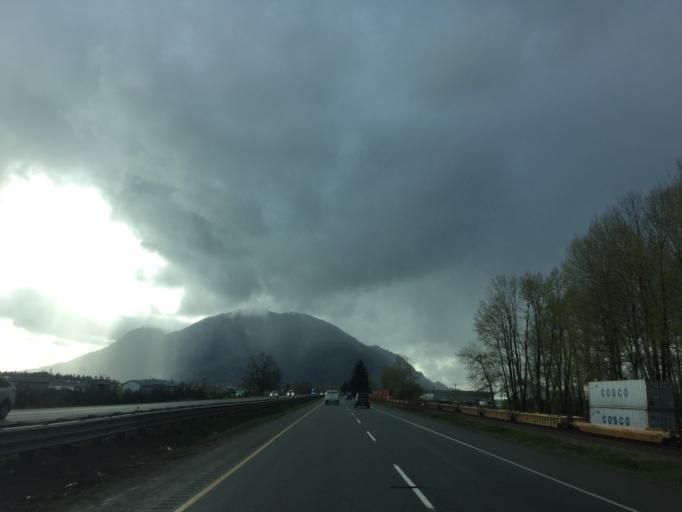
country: CA
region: British Columbia
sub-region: Fraser Valley Regional District
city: Chilliwack
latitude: 49.1409
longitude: -122.0413
